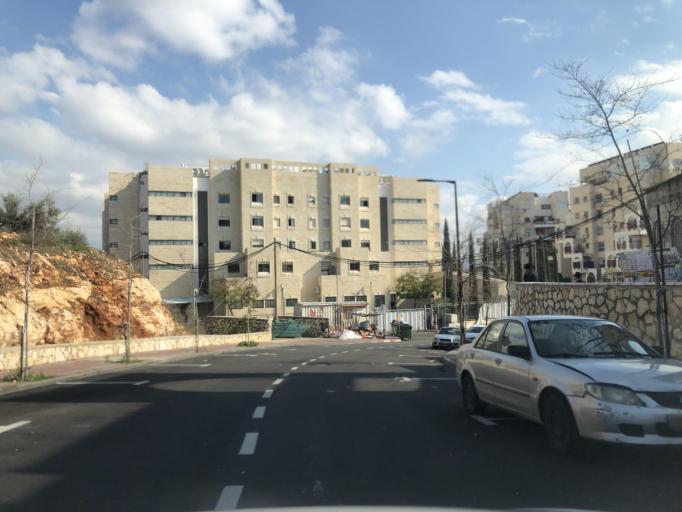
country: PS
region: West Bank
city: Dayr Qiddis
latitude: 31.9415
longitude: 35.0416
